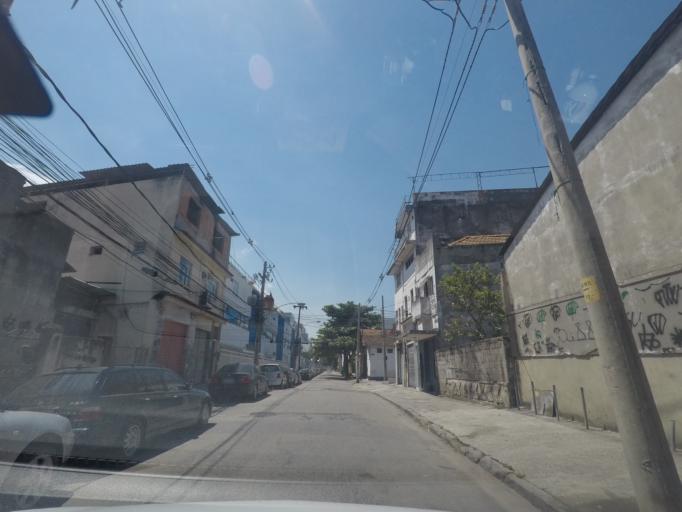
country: BR
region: Rio de Janeiro
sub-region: Rio De Janeiro
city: Rio de Janeiro
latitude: -22.9056
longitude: -43.2123
